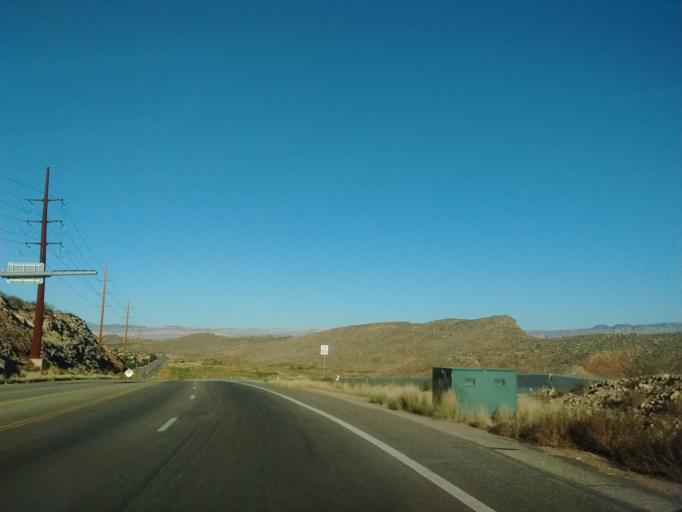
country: US
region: Utah
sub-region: Washington County
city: Washington
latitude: 37.1386
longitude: -113.4679
